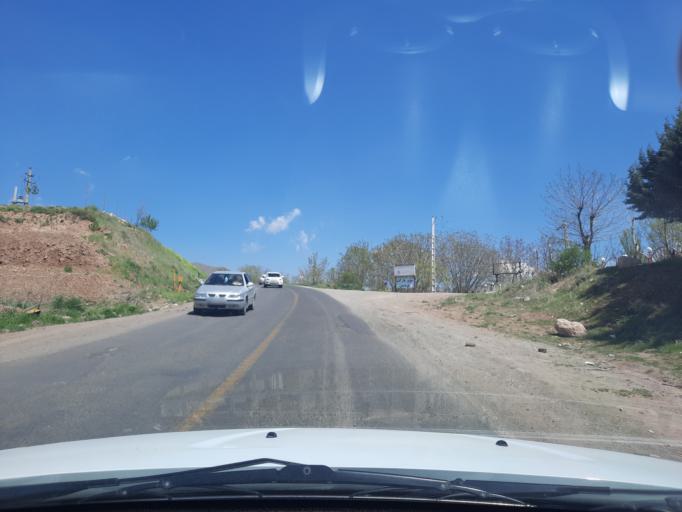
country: IR
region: Qazvin
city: Qazvin
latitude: 36.3416
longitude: 50.1711
